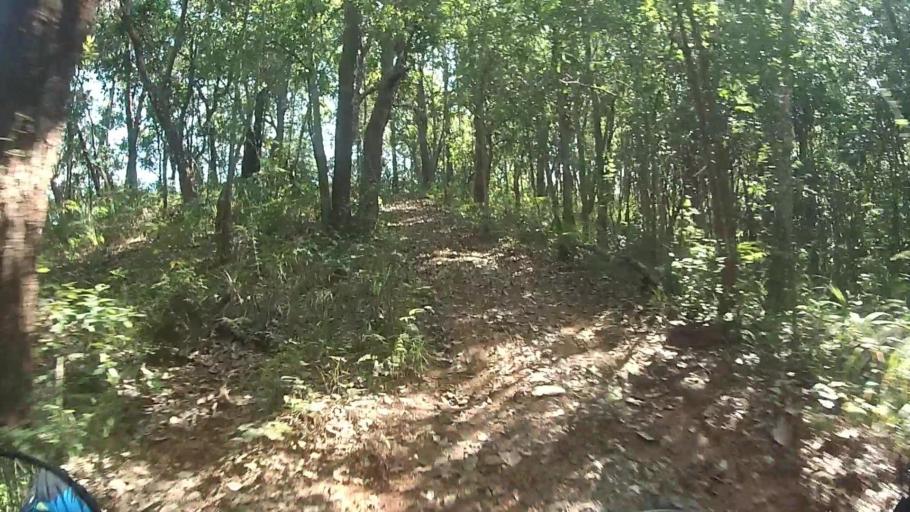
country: TH
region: Chiang Mai
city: Mae On
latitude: 19.0403
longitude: 99.2852
